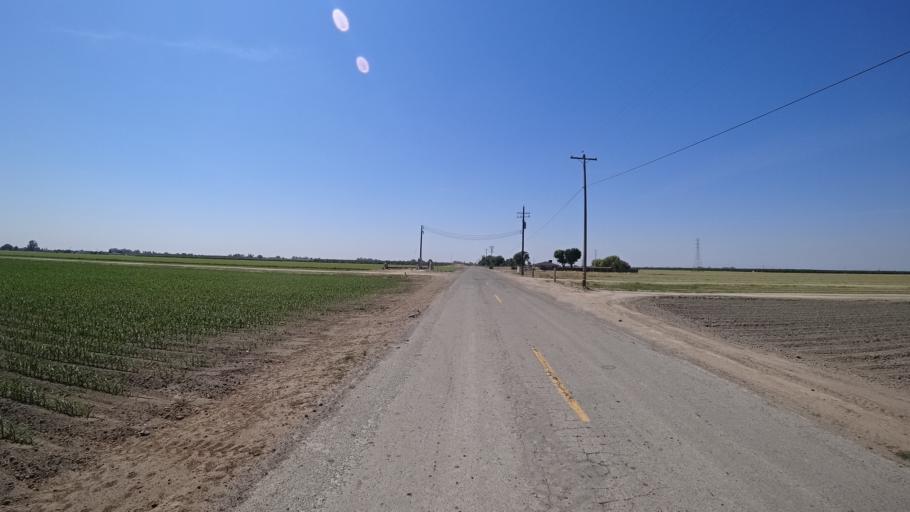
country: US
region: California
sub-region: Fresno County
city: Riverdale
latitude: 36.3988
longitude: -119.8872
